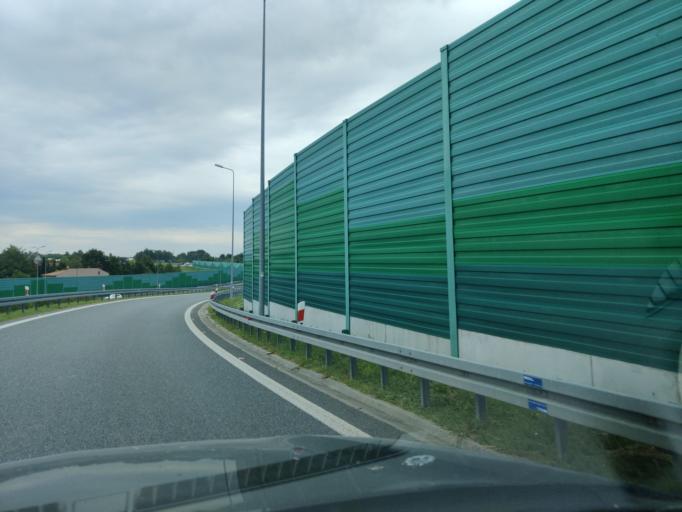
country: PL
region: Masovian Voivodeship
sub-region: Powiat minski
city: Minsk Mazowiecki
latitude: 52.2075
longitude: 21.5272
